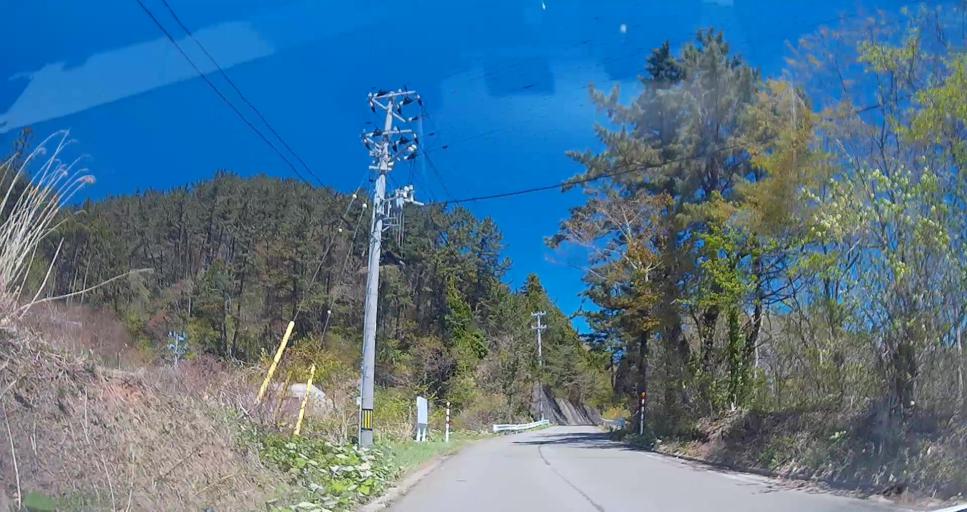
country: JP
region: Aomori
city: Mutsu
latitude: 41.1185
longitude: 141.3914
